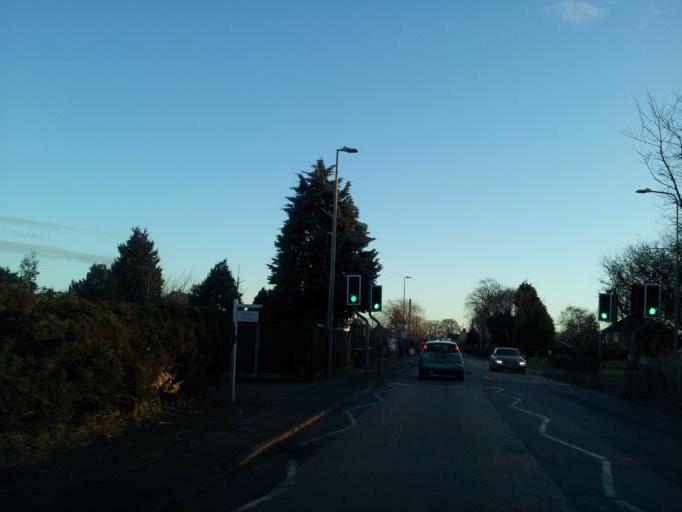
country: GB
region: England
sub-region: Lincolnshire
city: Sudbrooke
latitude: 53.2736
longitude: -0.4103
